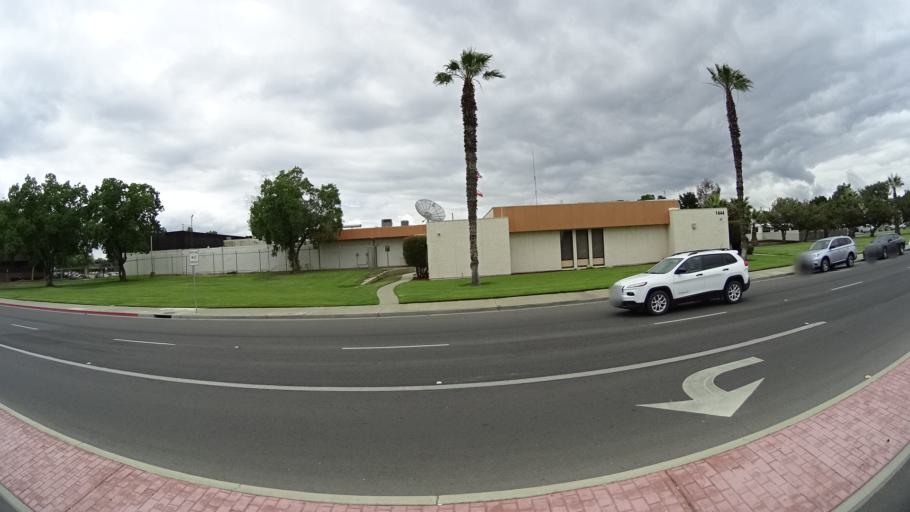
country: US
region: California
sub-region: Kings County
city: Hanford
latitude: 36.3280
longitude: -119.6677
